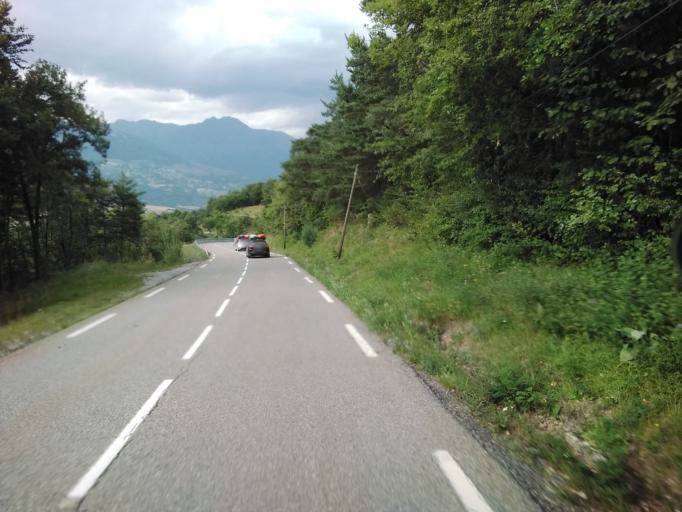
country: FR
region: Provence-Alpes-Cote d'Azur
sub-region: Departement des Hautes-Alpes
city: Chorges
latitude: 44.5025
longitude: 6.3484
